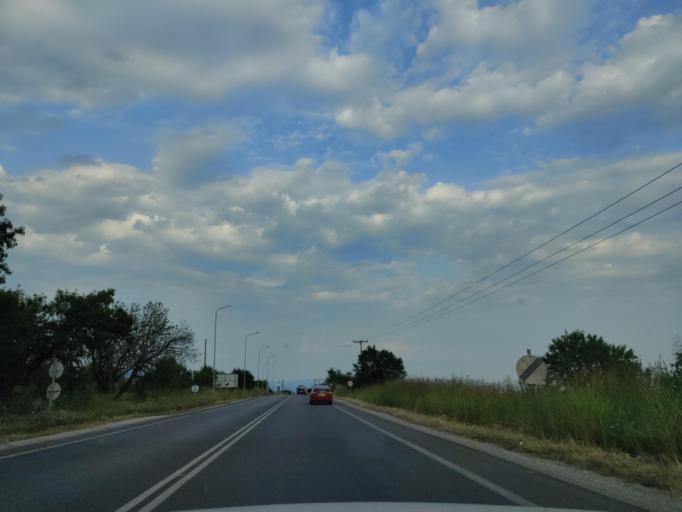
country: GR
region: East Macedonia and Thrace
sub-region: Nomos Dramas
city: Xiropotamos
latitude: 41.1627
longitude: 24.0753
